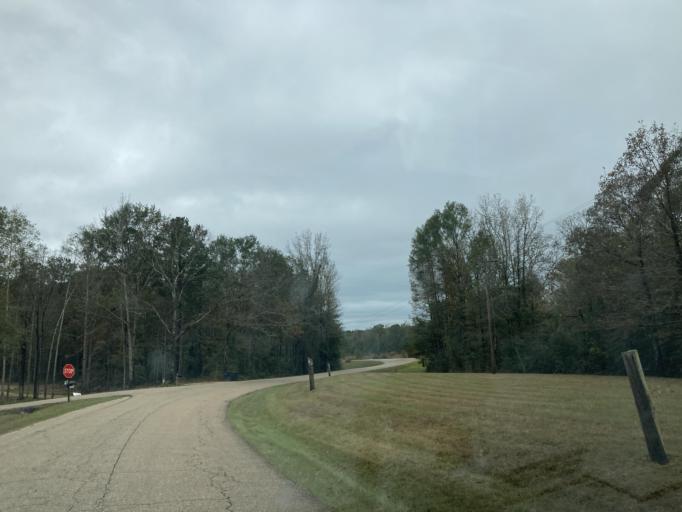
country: US
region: Mississippi
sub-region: Lamar County
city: West Hattiesburg
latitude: 31.2586
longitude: -89.4917
